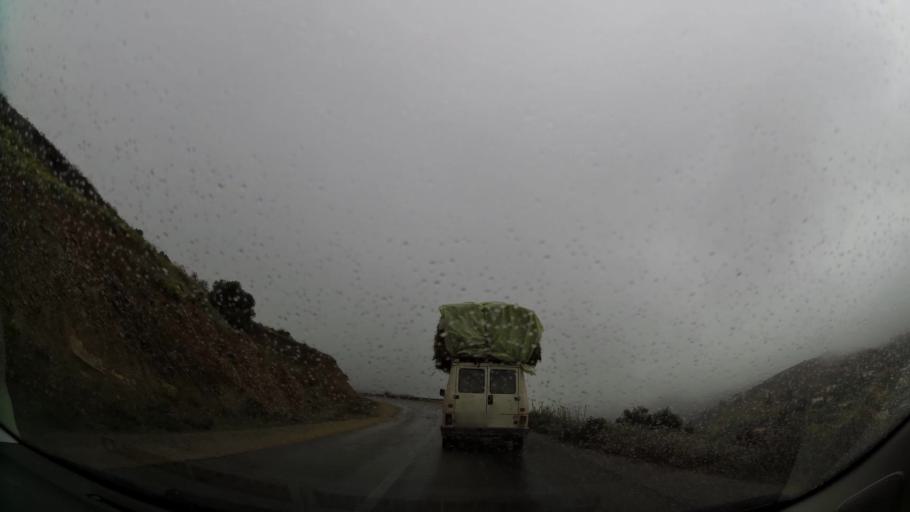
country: MA
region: Oriental
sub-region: Nador
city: Boudinar
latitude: 35.0934
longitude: -3.5237
